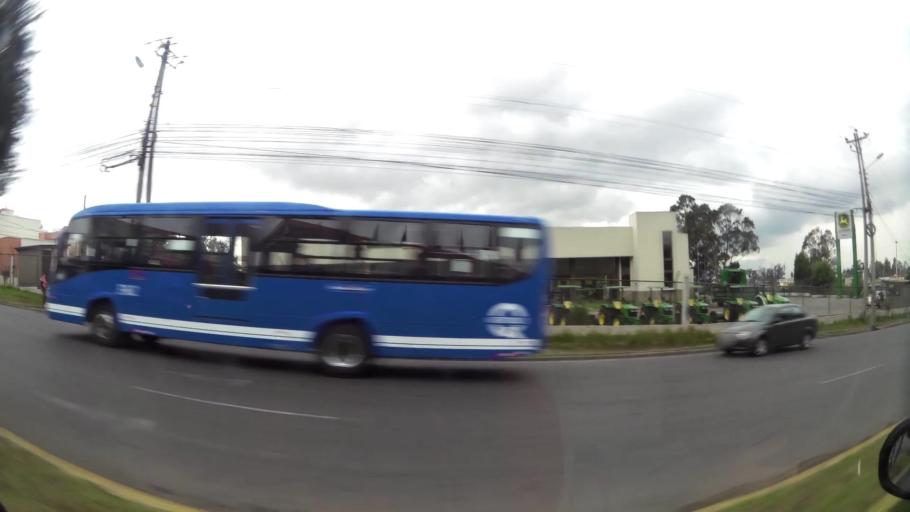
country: EC
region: Pichincha
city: Quito
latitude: -0.1077
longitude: -78.4617
